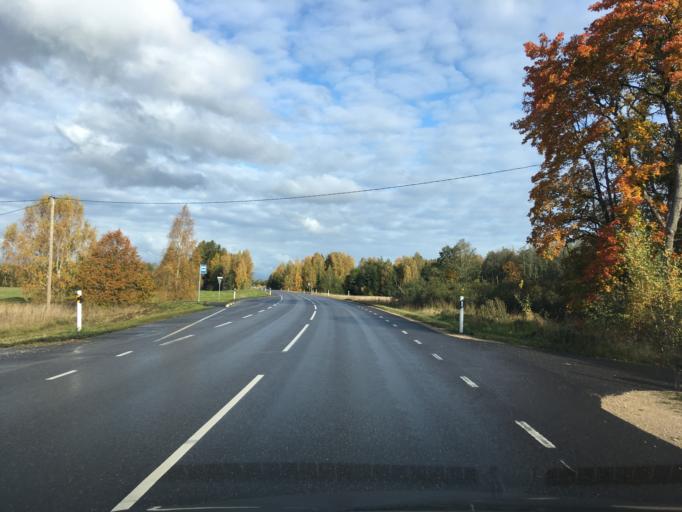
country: EE
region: Harju
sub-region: Raasiku vald
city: Raasiku
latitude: 59.1939
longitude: 25.1855
